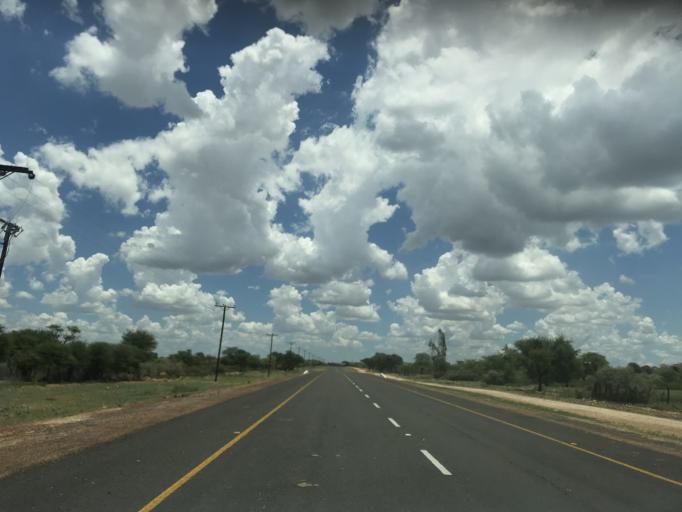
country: BW
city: Mabuli
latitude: -25.8038
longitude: 24.8262
